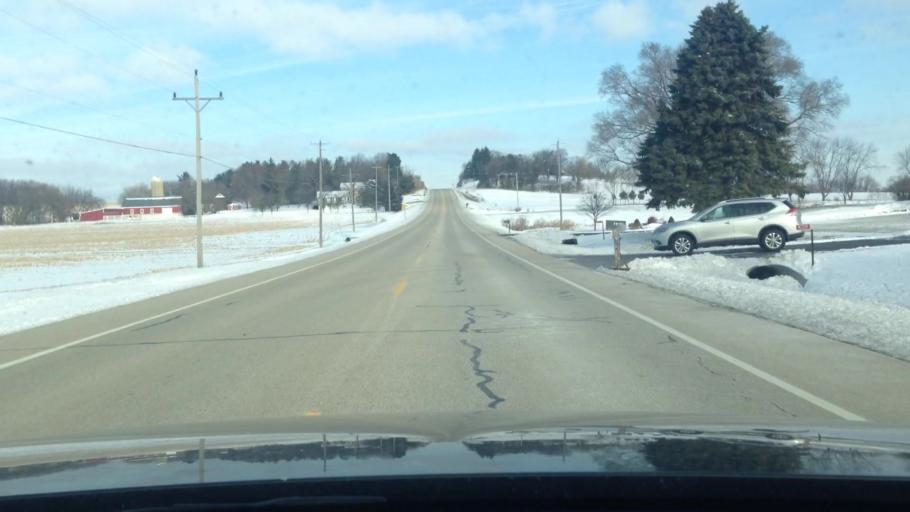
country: US
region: Wisconsin
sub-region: Walworth County
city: East Troy
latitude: 42.7527
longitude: -88.4064
